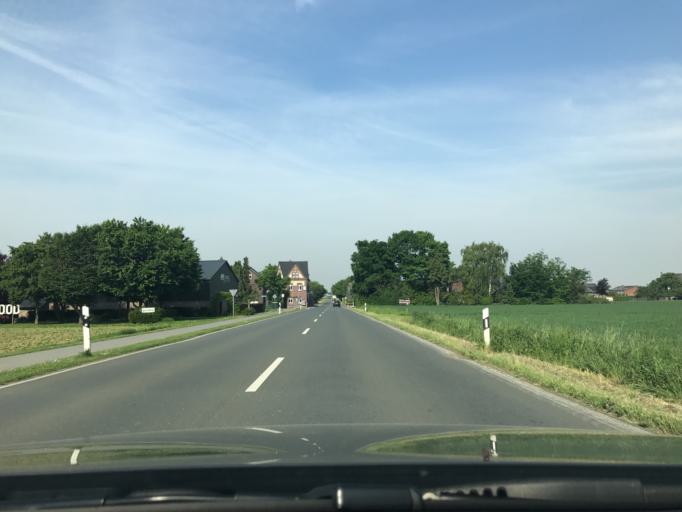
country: DE
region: North Rhine-Westphalia
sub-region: Regierungsbezirk Dusseldorf
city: Rheurdt
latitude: 51.4414
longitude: 6.4634
